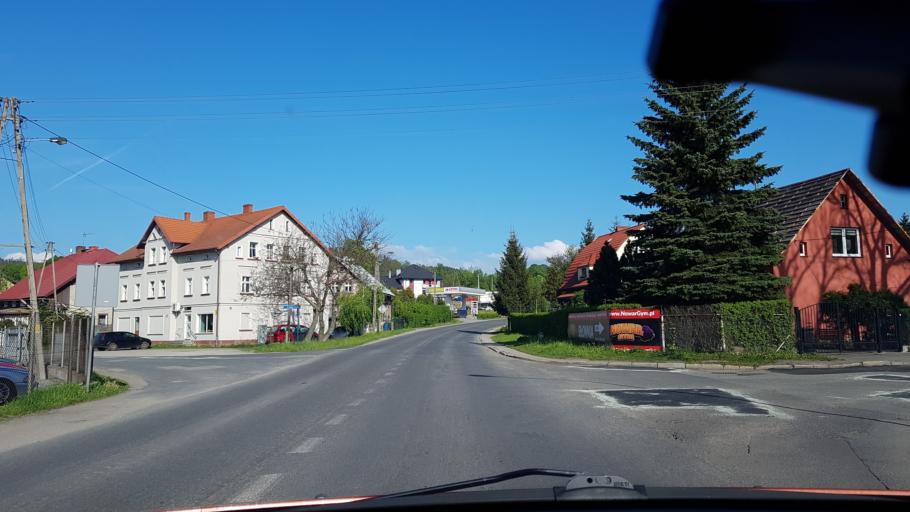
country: PL
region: Lower Silesian Voivodeship
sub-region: Powiat klodzki
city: Nowa Ruda
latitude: 50.5785
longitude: 16.5195
